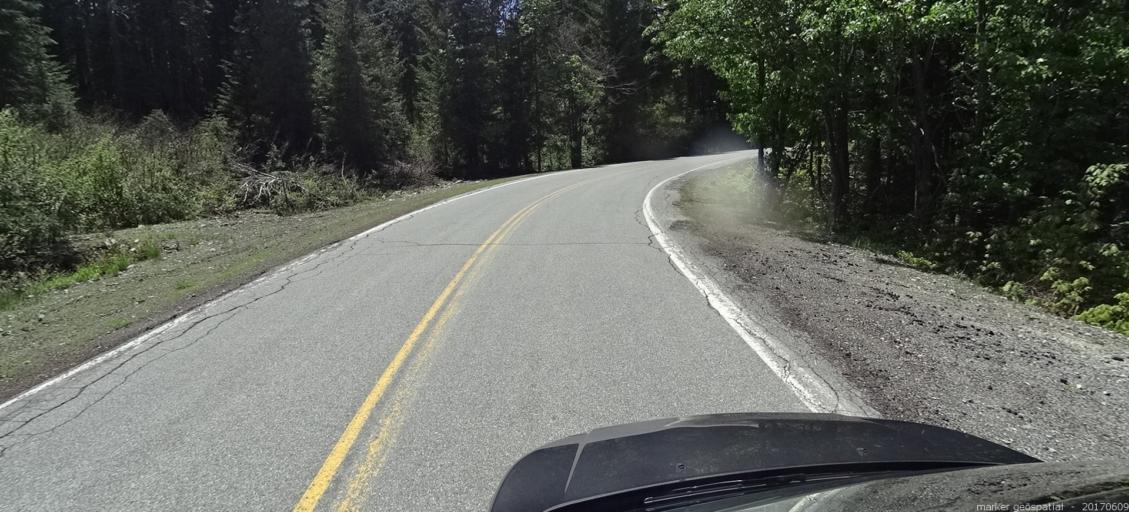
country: US
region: California
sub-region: Siskiyou County
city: Yreka
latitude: 41.4069
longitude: -122.9766
